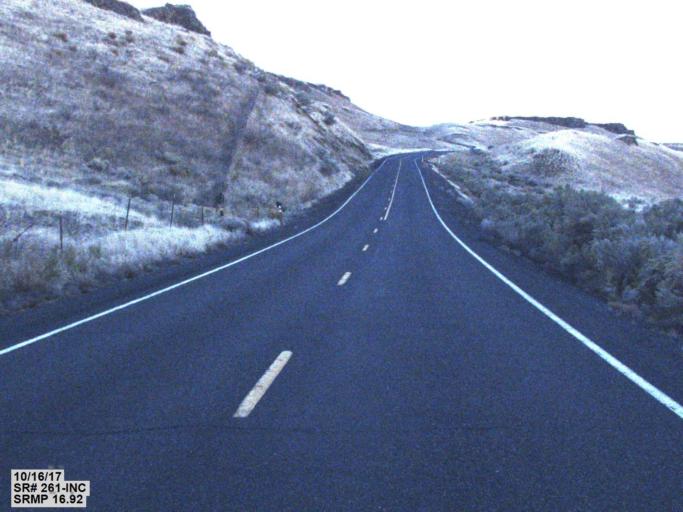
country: US
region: Washington
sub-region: Walla Walla County
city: Waitsburg
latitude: 46.6131
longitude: -118.2271
